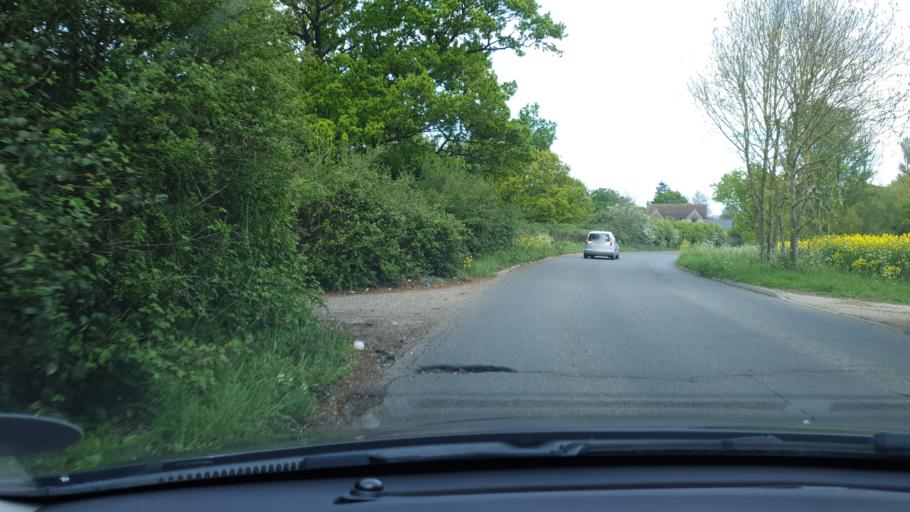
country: GB
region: England
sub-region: Essex
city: Great Bentley
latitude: 51.8935
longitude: 1.0678
